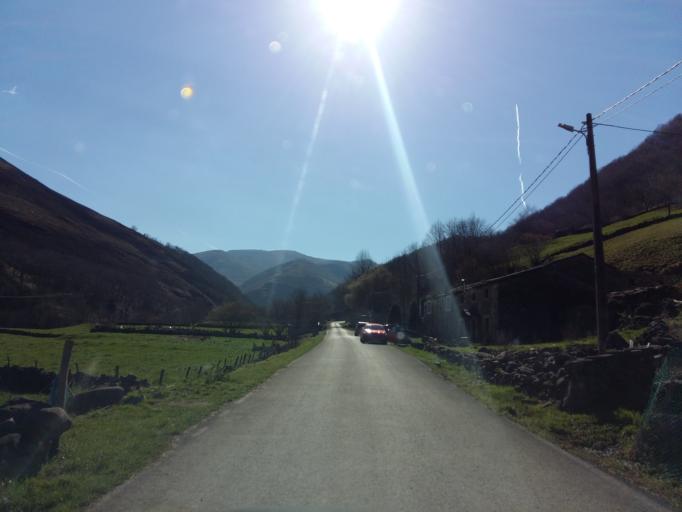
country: ES
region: Cantabria
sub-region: Provincia de Cantabria
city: Vega de Pas
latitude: 43.1449
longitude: -3.7984
